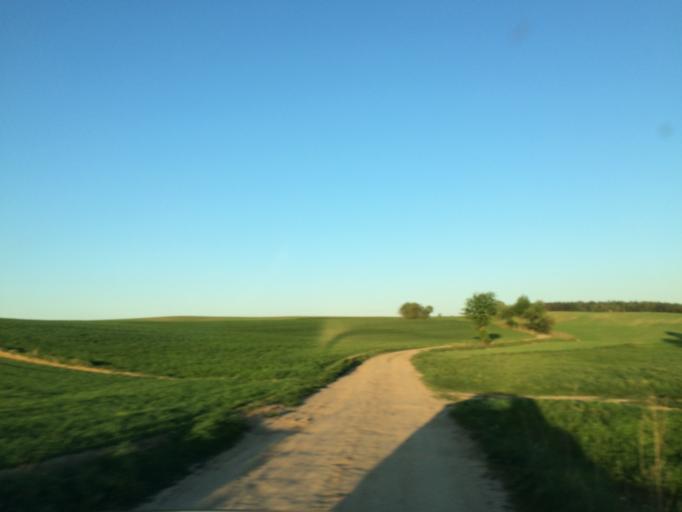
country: PL
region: Warmian-Masurian Voivodeship
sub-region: Powiat ilawski
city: Lubawa
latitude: 53.4902
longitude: 19.8475
